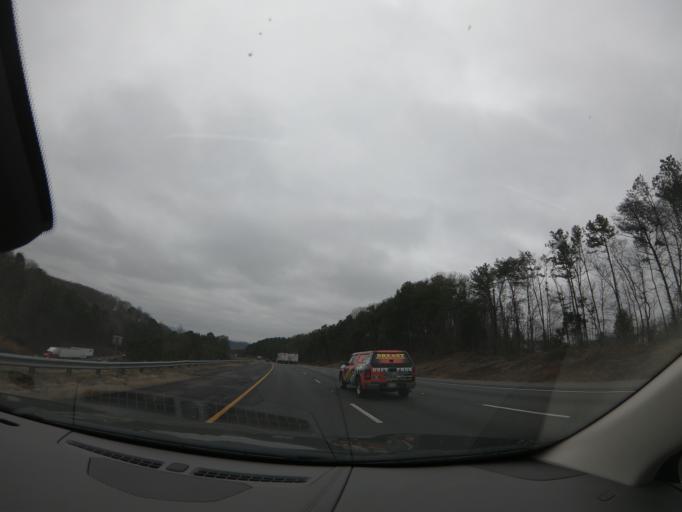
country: US
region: Georgia
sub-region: Catoosa County
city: Indian Springs
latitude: 34.9362
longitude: -85.1572
